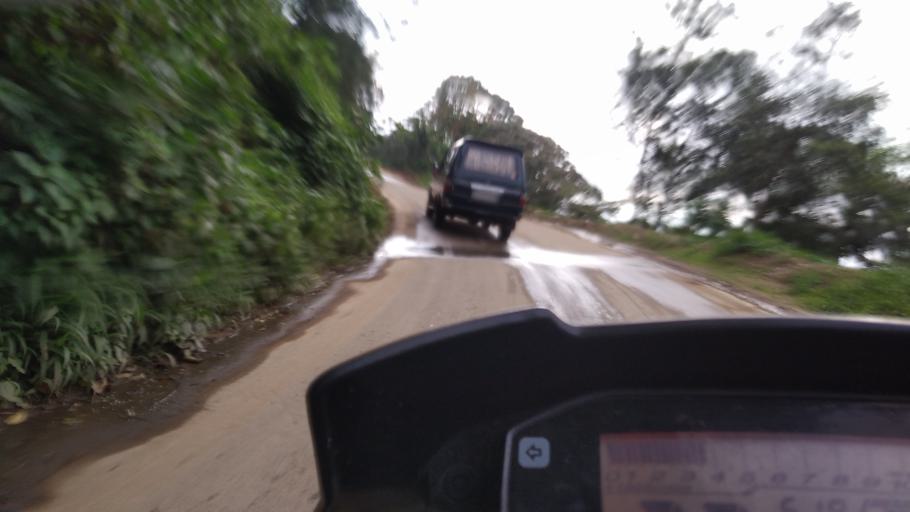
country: IN
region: Tamil Nadu
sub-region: Theni
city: Bodinayakkanur
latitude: 10.0207
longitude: 77.2470
